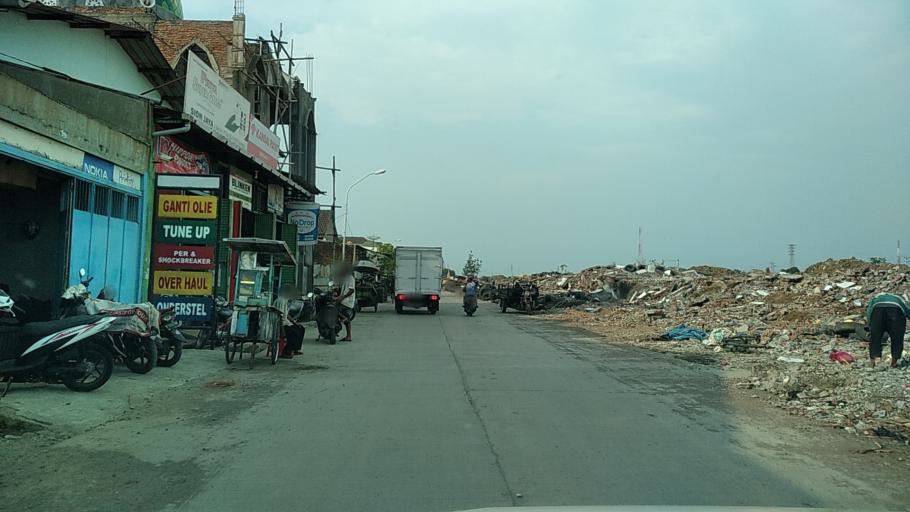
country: ID
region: Central Java
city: Semarang
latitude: -6.9710
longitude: 110.4424
